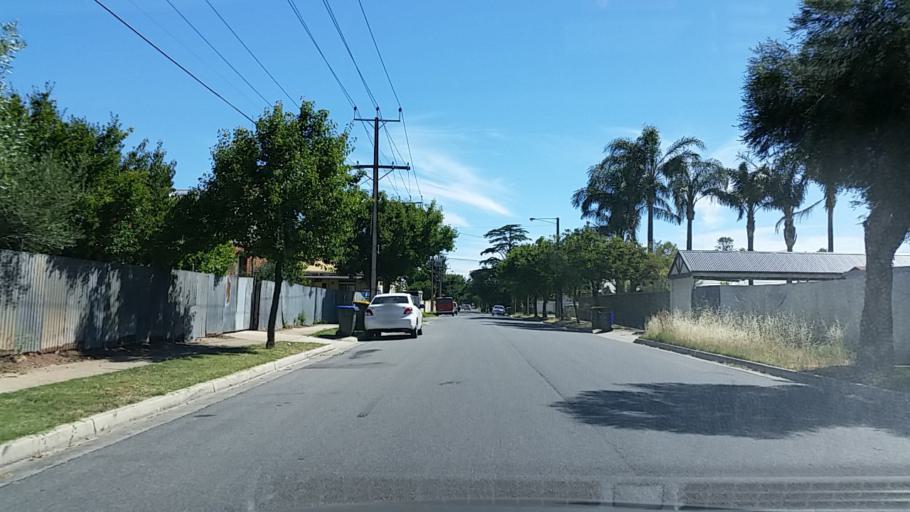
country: AU
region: South Australia
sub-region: Charles Sturt
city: Allenby Gardens
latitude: -34.8892
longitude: 138.5618
